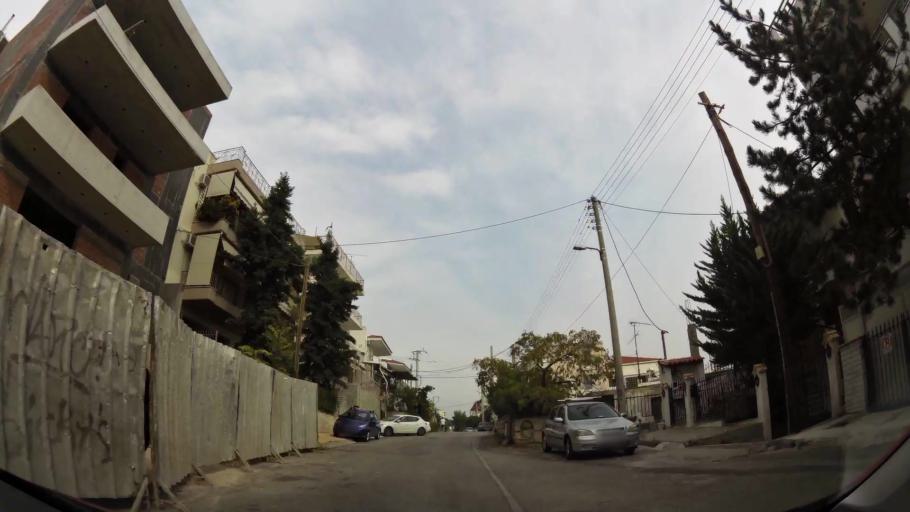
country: GR
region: Attica
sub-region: Nomarchia Athinas
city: Chaidari
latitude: 38.0202
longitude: 23.6452
